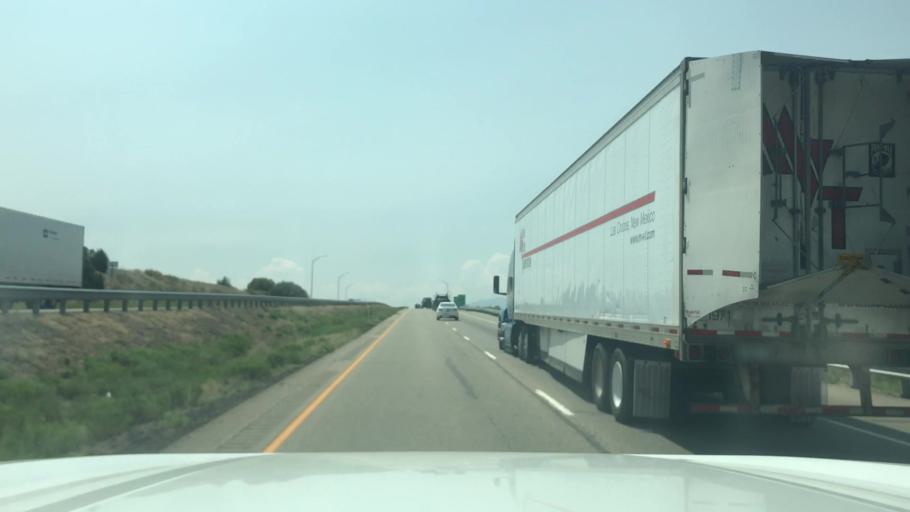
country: US
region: Colorado
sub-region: Pueblo County
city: Colorado City
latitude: 37.9675
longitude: -104.7896
